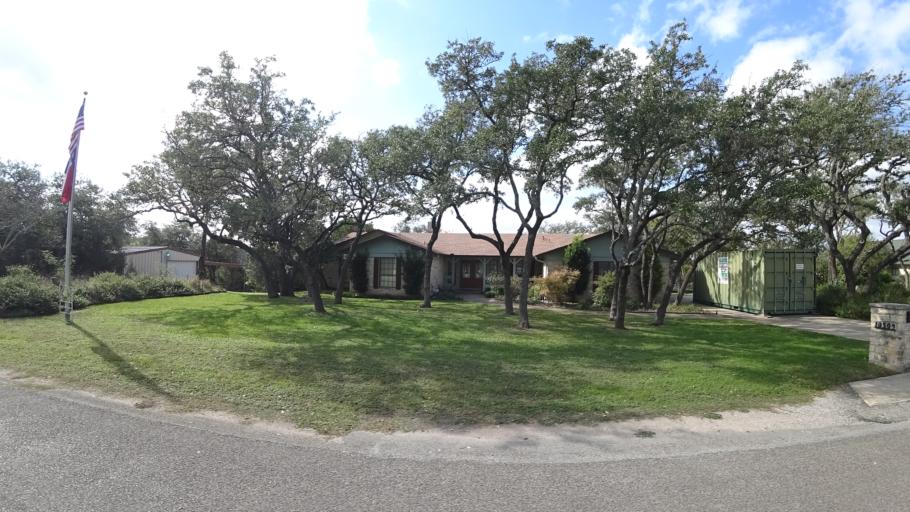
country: US
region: Texas
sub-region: Travis County
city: Bee Cave
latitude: 30.2535
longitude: -97.9334
